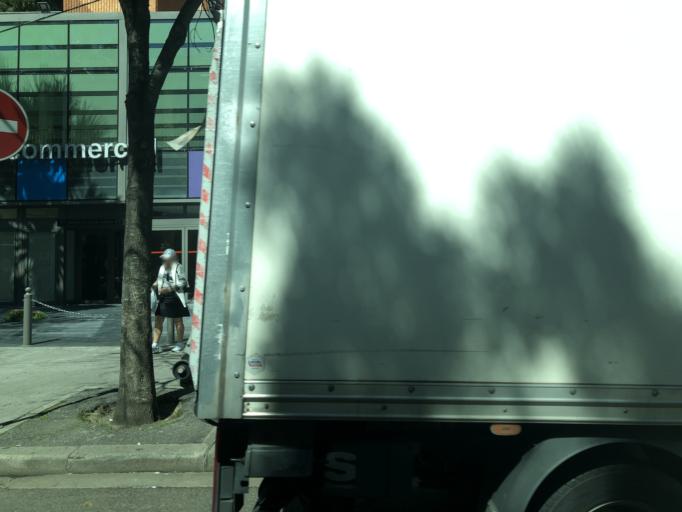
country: FR
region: Provence-Alpes-Cote d'Azur
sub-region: Departement des Alpes-Maritimes
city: Nice
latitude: 43.7053
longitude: 7.2855
